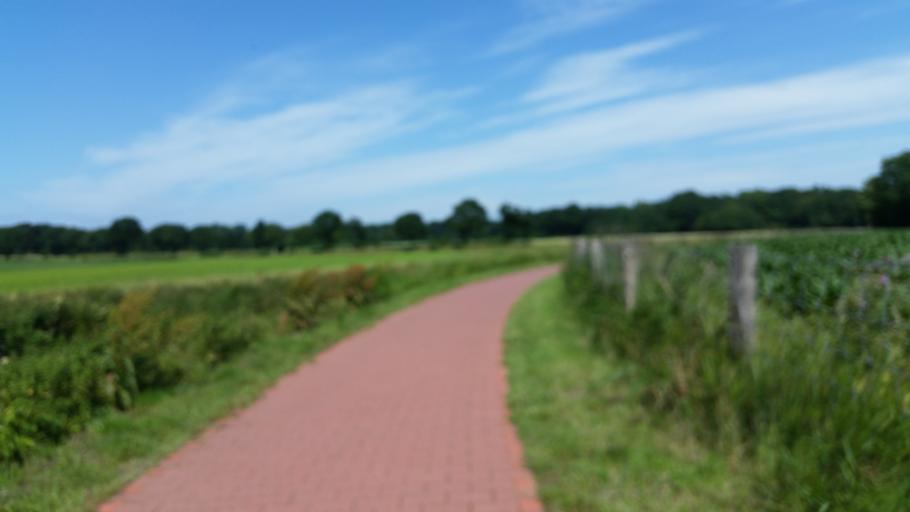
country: DE
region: Lower Saxony
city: Aurich
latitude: 53.4795
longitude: 7.4615
